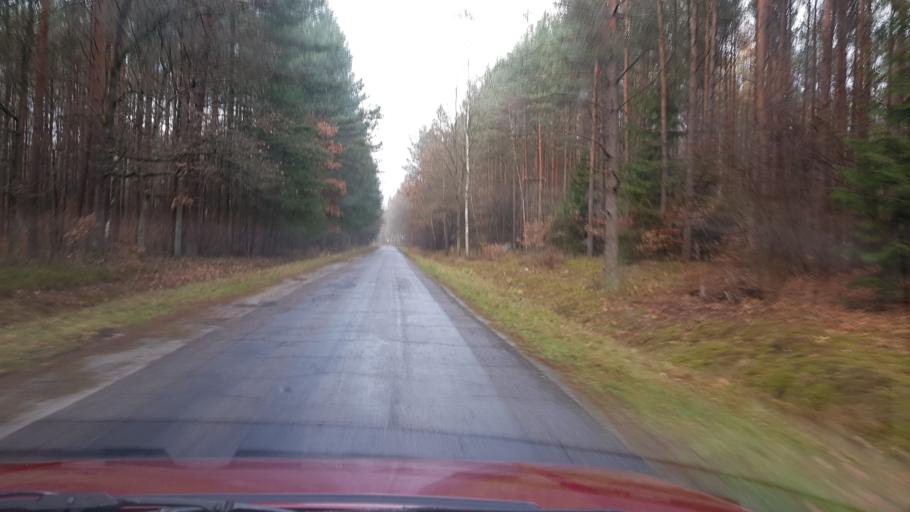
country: PL
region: West Pomeranian Voivodeship
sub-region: Powiat bialogardzki
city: Tychowo
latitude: 53.9726
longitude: 16.3144
